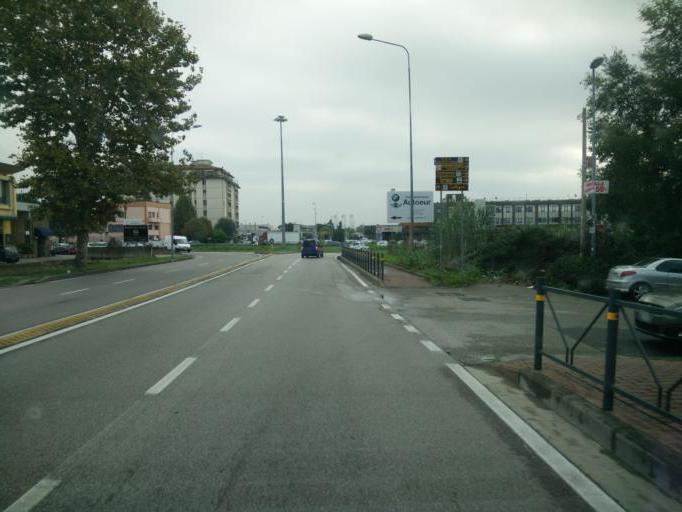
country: IT
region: Tuscany
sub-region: Province of Florence
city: Mantignano-Ugnano
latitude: 43.8041
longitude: 11.1832
